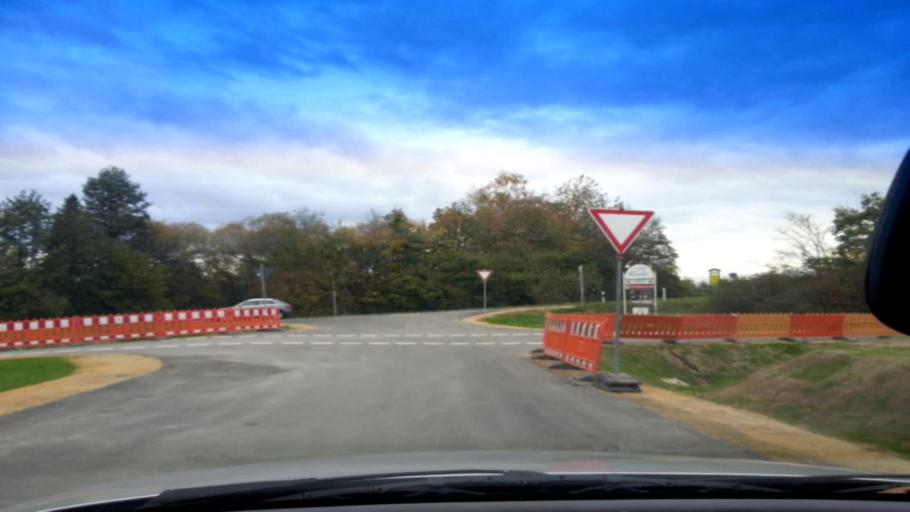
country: DE
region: Bavaria
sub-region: Upper Franconia
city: Kemmern
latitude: 49.9557
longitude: 10.8840
